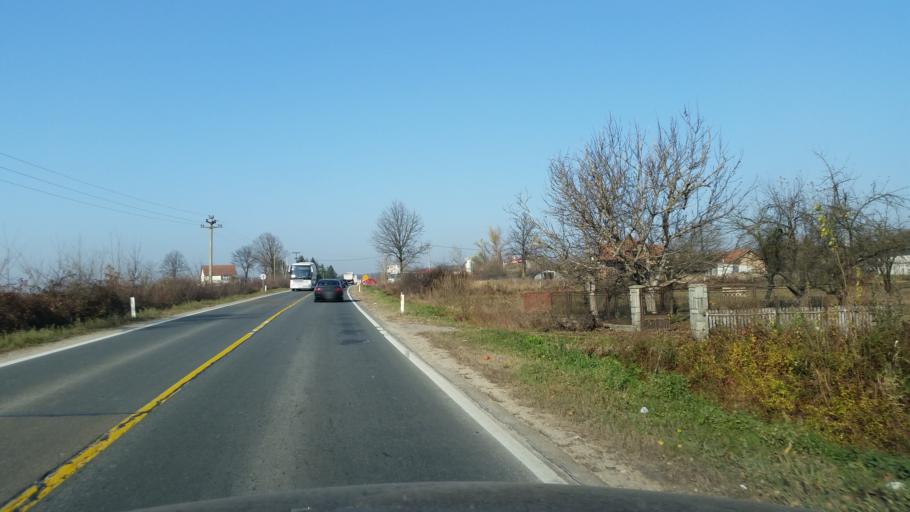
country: RS
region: Central Serbia
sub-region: Kolubarski Okrug
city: Ljig
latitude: 44.2980
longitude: 20.2607
